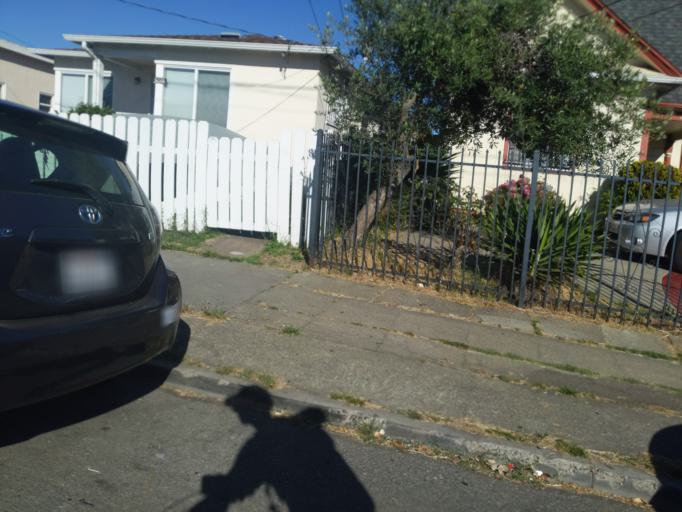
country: US
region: California
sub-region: Alameda County
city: Piedmont
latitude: 37.7921
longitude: -122.2145
